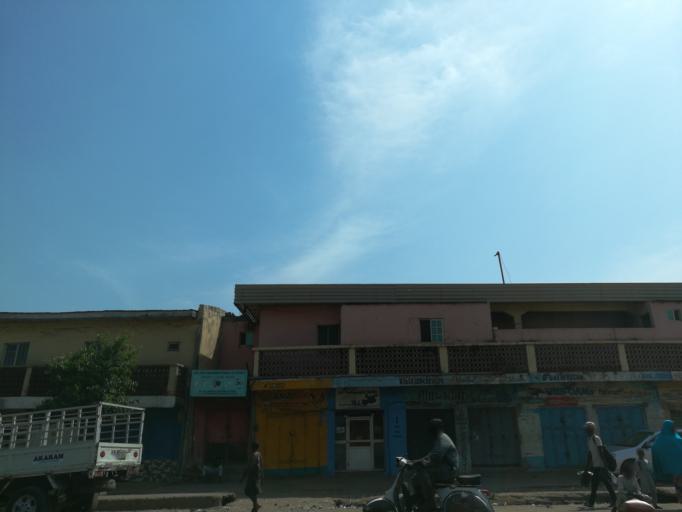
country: NG
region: Kano
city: Kano
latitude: 12.0154
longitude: 8.5145
